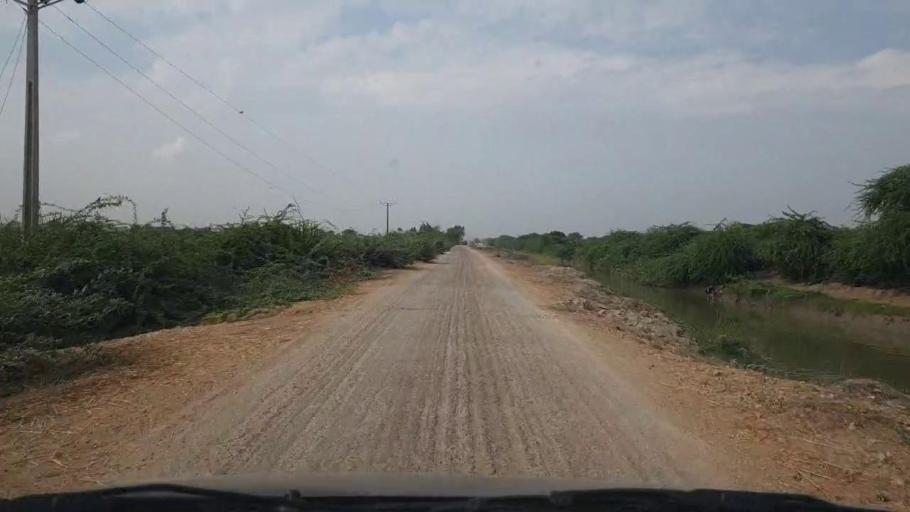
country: PK
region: Sindh
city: Kario
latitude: 24.6285
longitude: 68.5741
